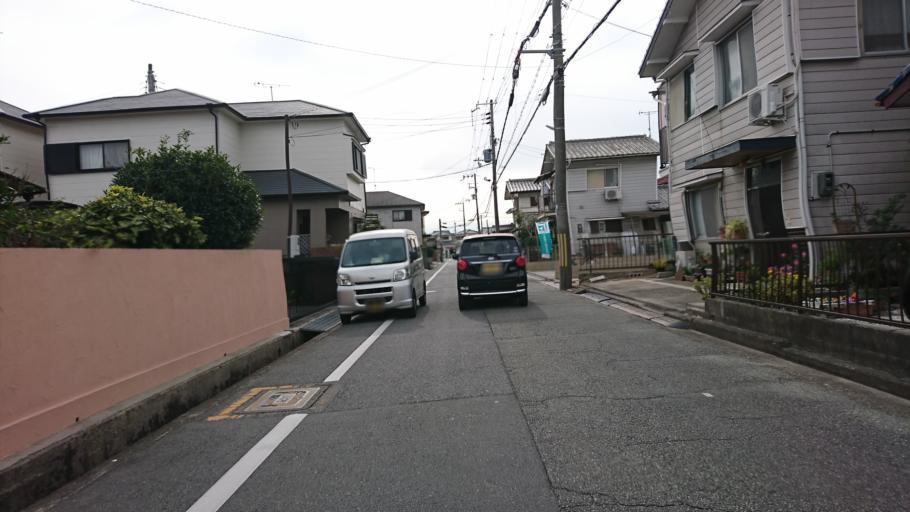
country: JP
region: Hyogo
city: Kakogawacho-honmachi
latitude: 34.7764
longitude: 134.8569
